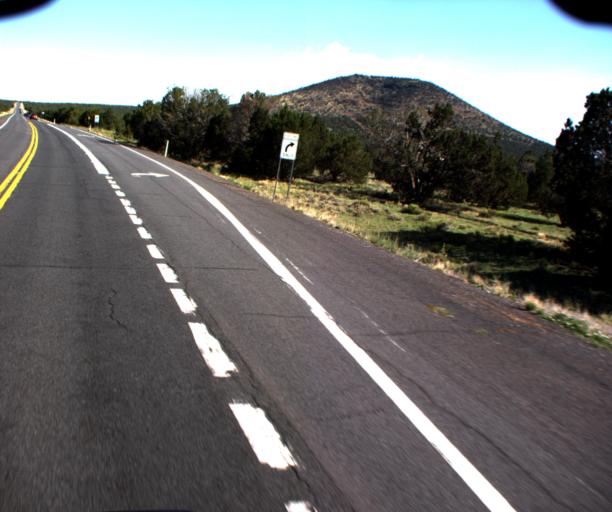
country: US
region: Arizona
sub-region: Coconino County
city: Williams
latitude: 35.3803
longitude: -112.1618
